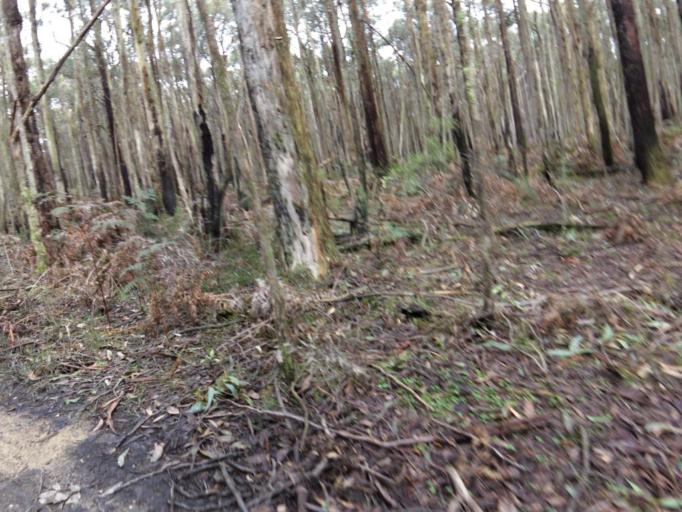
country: AU
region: Victoria
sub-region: Moorabool
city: Bacchus Marsh
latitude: -37.4294
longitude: 144.4733
